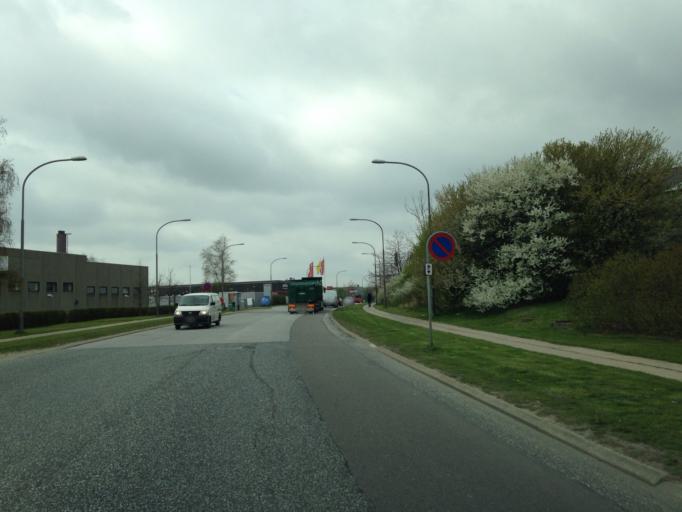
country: DK
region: Capital Region
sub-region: Ishoj Kommune
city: Ishoj
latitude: 55.6190
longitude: 12.3342
